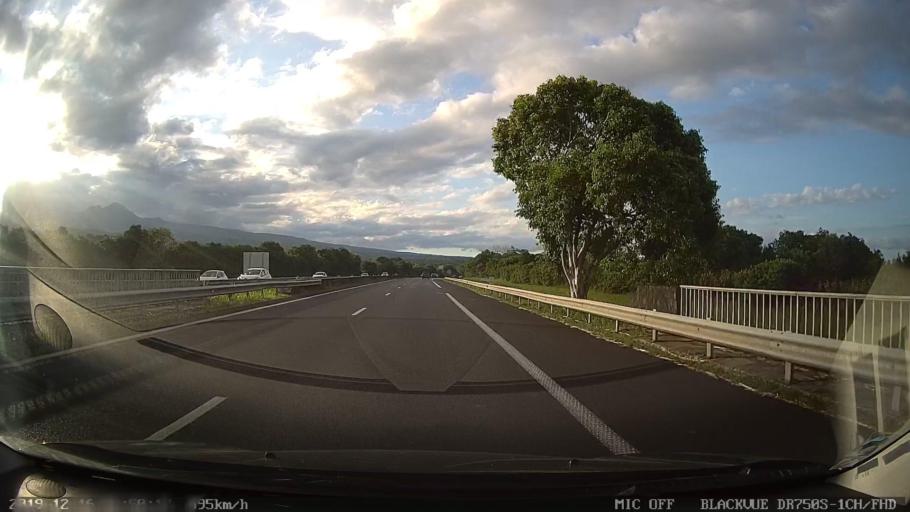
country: RE
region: Reunion
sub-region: Reunion
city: Bras-Panon
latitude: -21.0149
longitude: 55.6923
